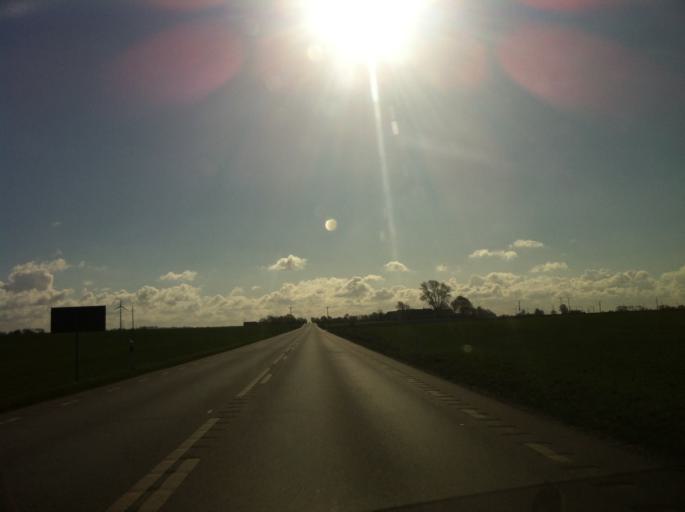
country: SE
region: Skane
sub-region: Svalovs Kommun
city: Teckomatorp
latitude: 55.8764
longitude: 13.0632
